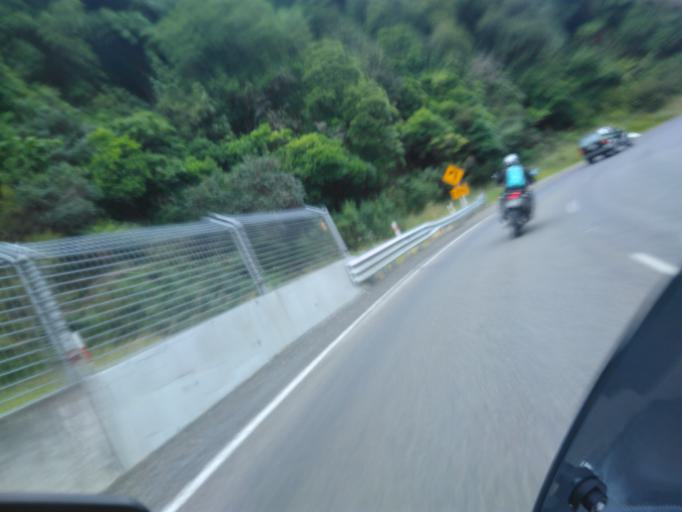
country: NZ
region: Bay of Plenty
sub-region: Opotiki District
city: Opotiki
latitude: -38.3120
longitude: 177.3960
